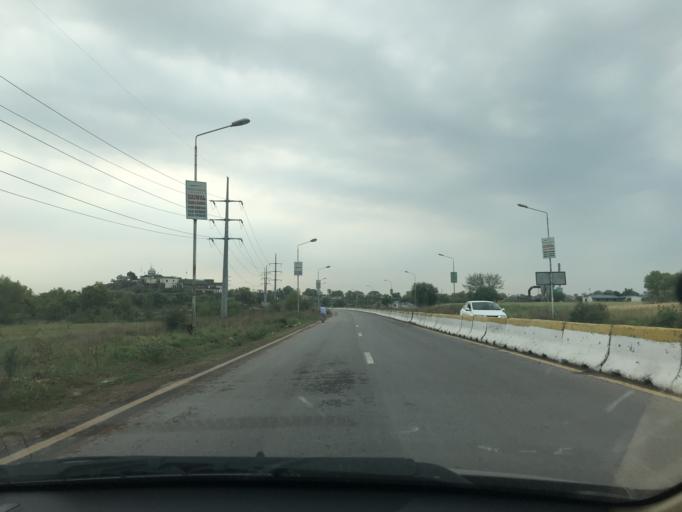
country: PK
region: Islamabad
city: Islamabad
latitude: 33.6956
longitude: 73.1773
